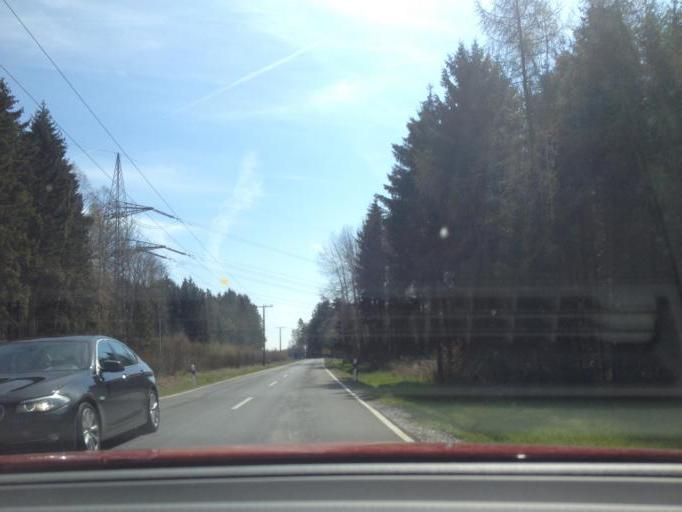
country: DE
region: Bavaria
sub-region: Upper Franconia
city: Hochstadt bei Thiersheim
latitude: 50.0753
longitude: 12.0814
